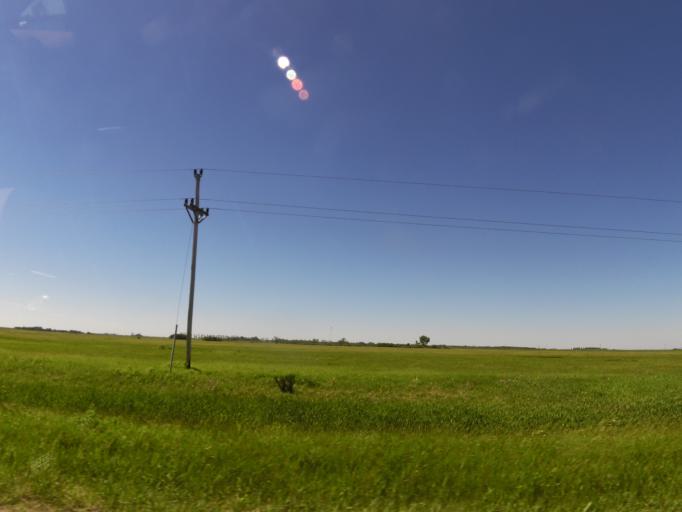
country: US
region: Minnesota
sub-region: Red Lake County
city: Red Lake Falls
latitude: 47.7574
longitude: -96.2605
